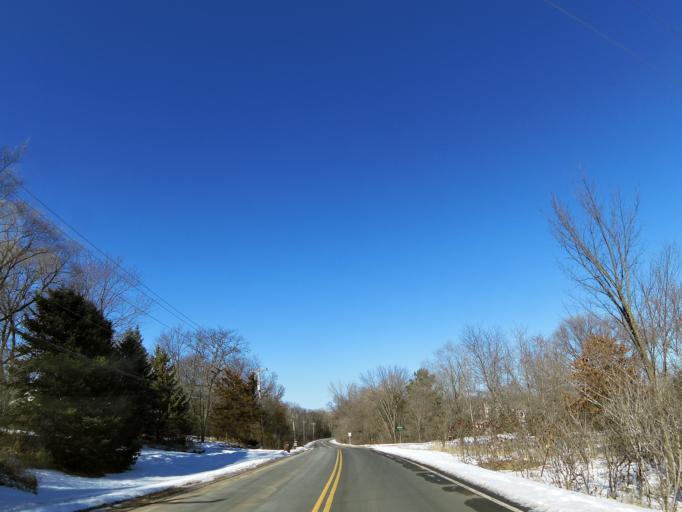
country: US
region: Minnesota
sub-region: Washington County
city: Lake Elmo
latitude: 44.9737
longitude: -92.8615
